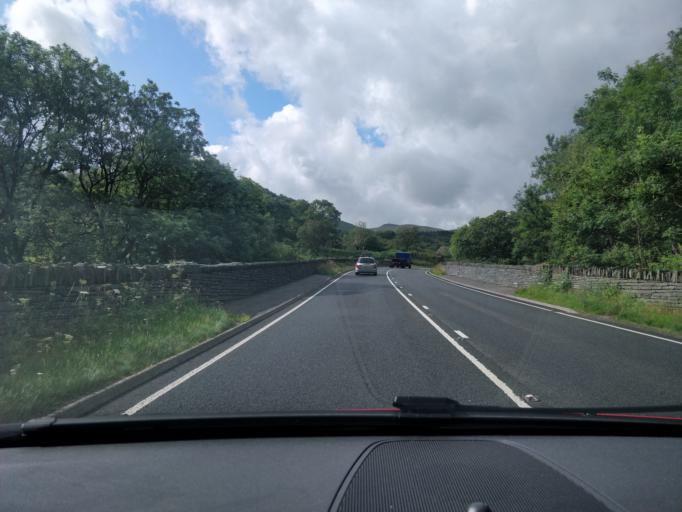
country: GB
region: Wales
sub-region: Gwynedd
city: Blaenau-Ffestiniog
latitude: 53.0468
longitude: -3.9096
